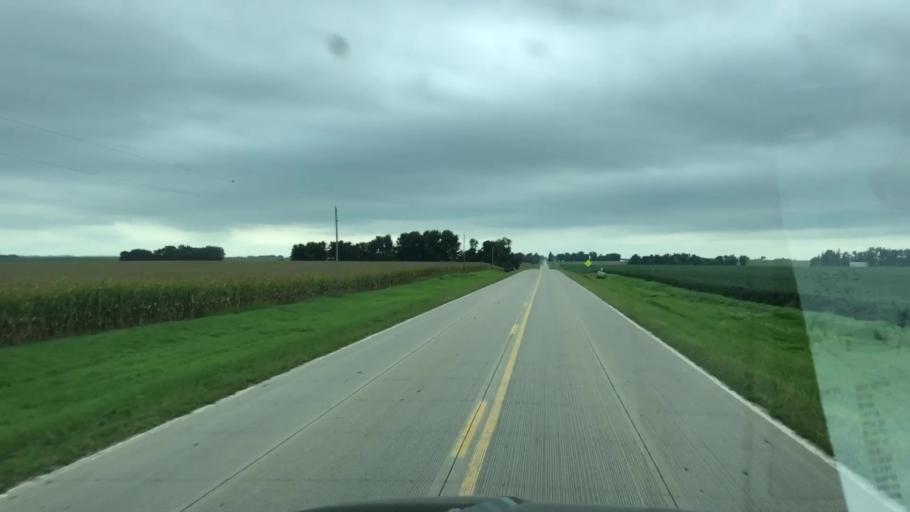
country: US
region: Iowa
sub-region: O'Brien County
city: Sheldon
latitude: 43.1237
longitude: -95.9789
